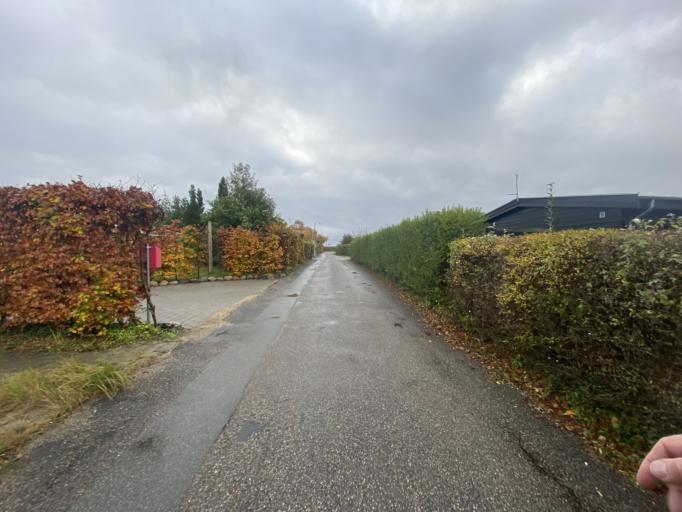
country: DK
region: Capital Region
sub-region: Dragor Kommune
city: Dragor
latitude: 55.5792
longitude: 12.6360
